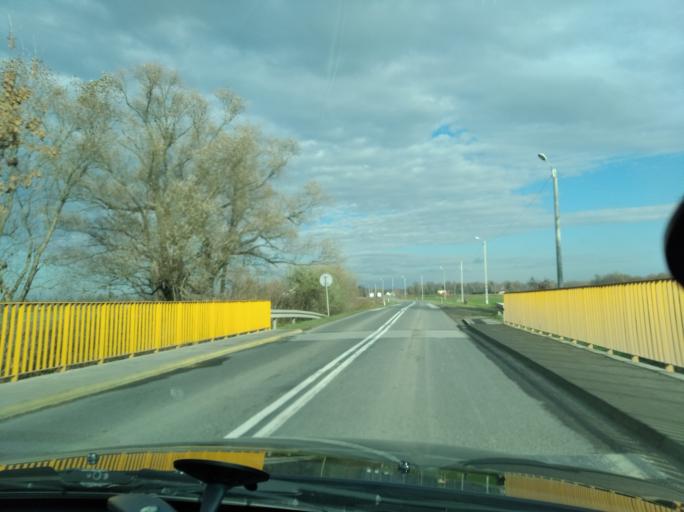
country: PL
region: Subcarpathian Voivodeship
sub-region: Powiat ropczycko-sedziszowski
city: Ostrow
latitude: 50.0890
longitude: 21.5907
